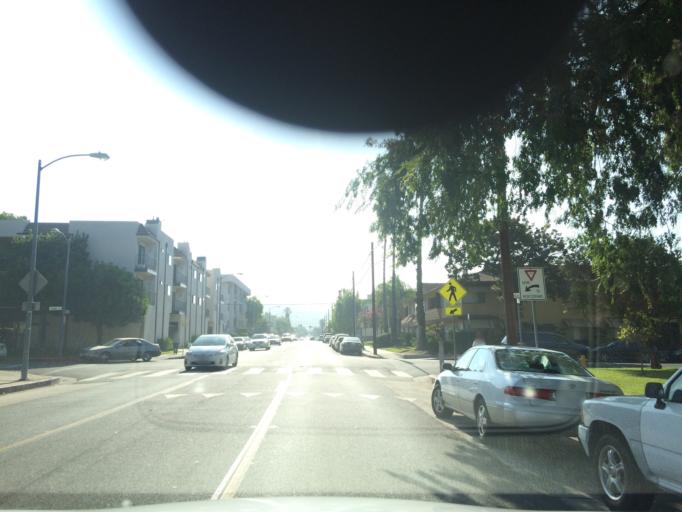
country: US
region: California
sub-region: Los Angeles County
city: Glendale
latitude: 34.1481
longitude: -118.2447
